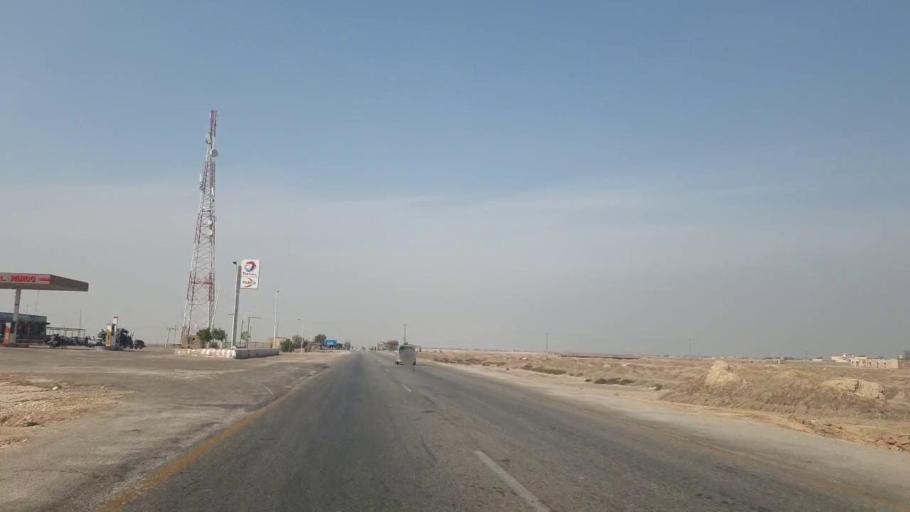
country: PK
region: Sindh
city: Sann
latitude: 25.9003
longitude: 68.2329
